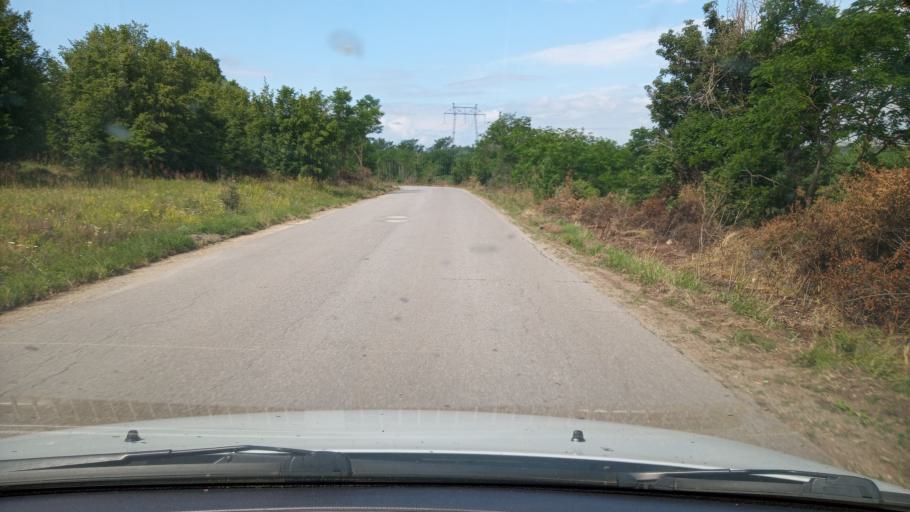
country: BG
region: Lovech
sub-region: Obshtina Lukovit
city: Lukovit
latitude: 43.1829
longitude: 24.0834
